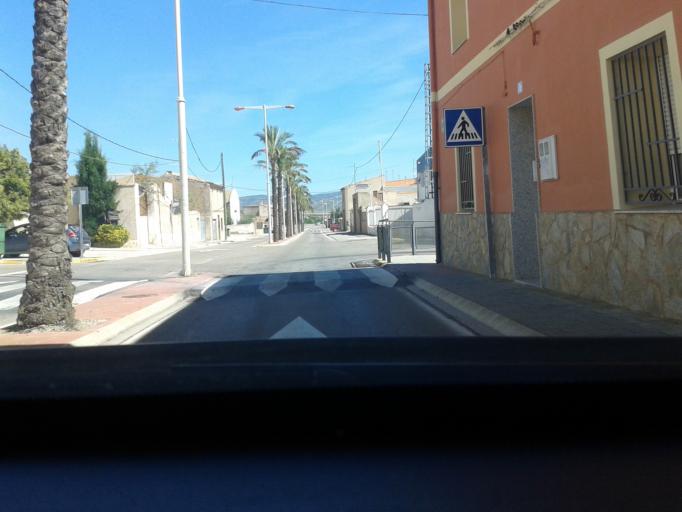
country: ES
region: Castille-La Mancha
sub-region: Provincia de Albacete
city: Caudete
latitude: 38.7086
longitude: -0.9829
